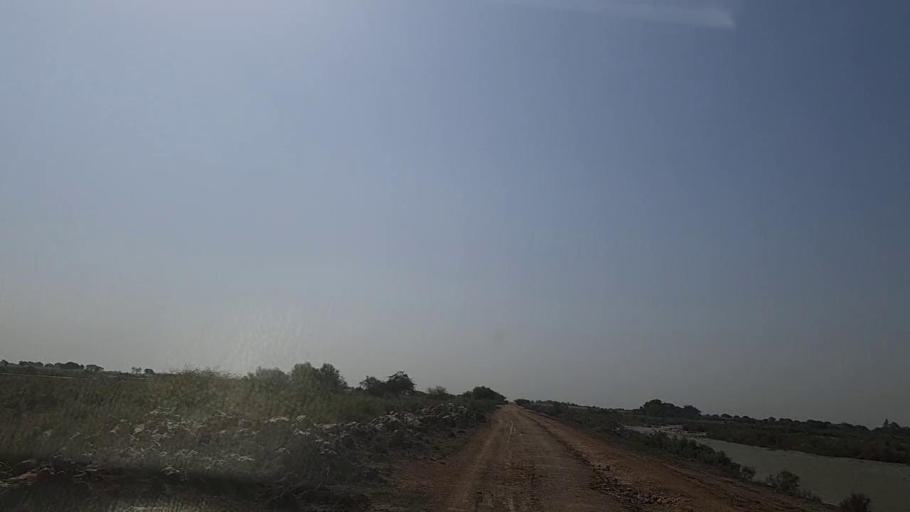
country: PK
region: Sindh
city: Daro Mehar
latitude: 24.7025
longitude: 68.1284
